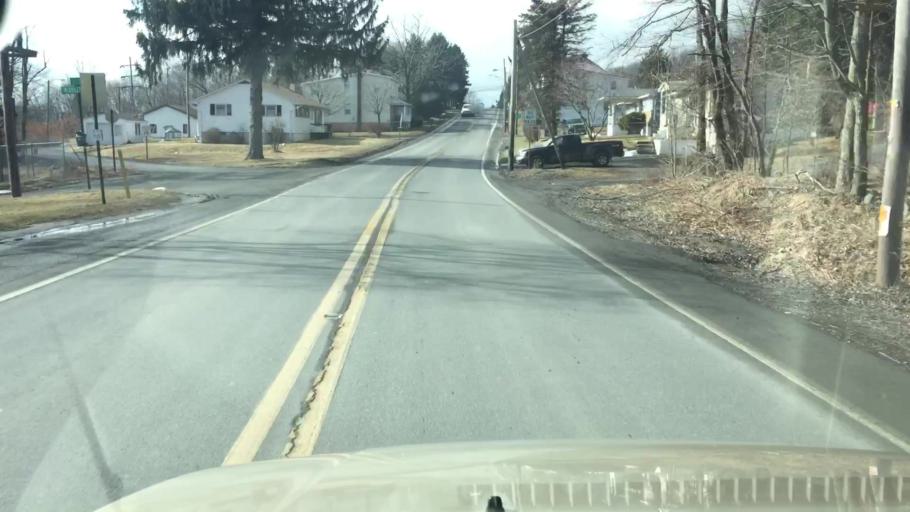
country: US
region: Pennsylvania
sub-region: Luzerne County
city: Oakdale
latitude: 40.9923
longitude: -75.9166
